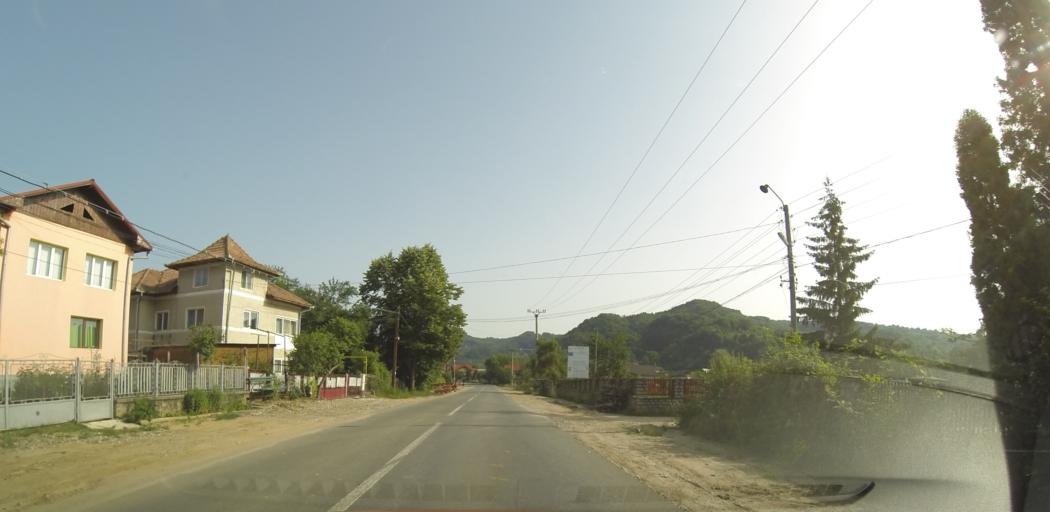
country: RO
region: Valcea
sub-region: Oras Baile Olanesti
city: Olanesti
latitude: 45.1712
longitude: 24.2579
